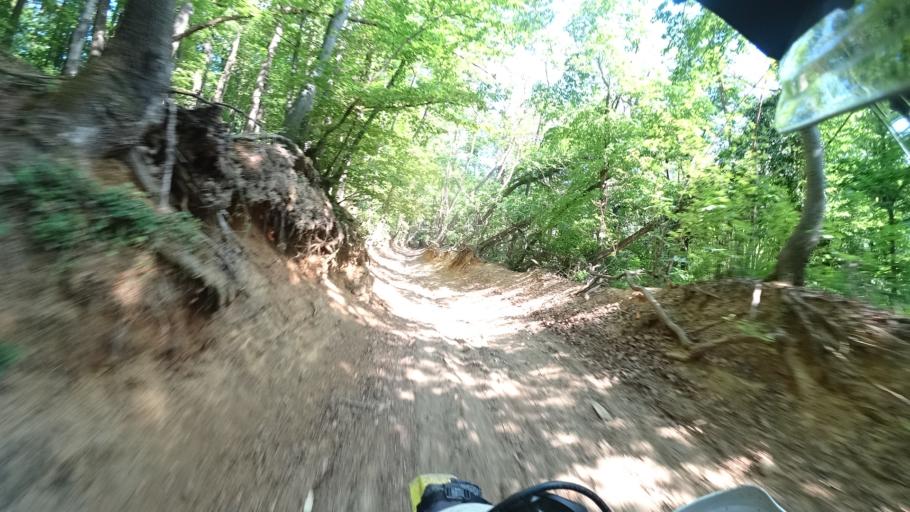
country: HR
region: Zagrebacka
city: Jablanovec
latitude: 45.8775
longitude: 15.8737
